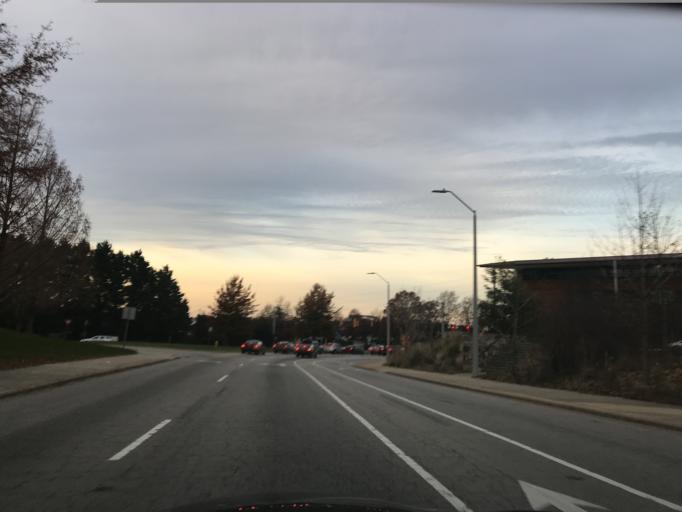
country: US
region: North Carolina
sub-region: Wake County
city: Raleigh
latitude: 35.7871
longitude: -78.6381
